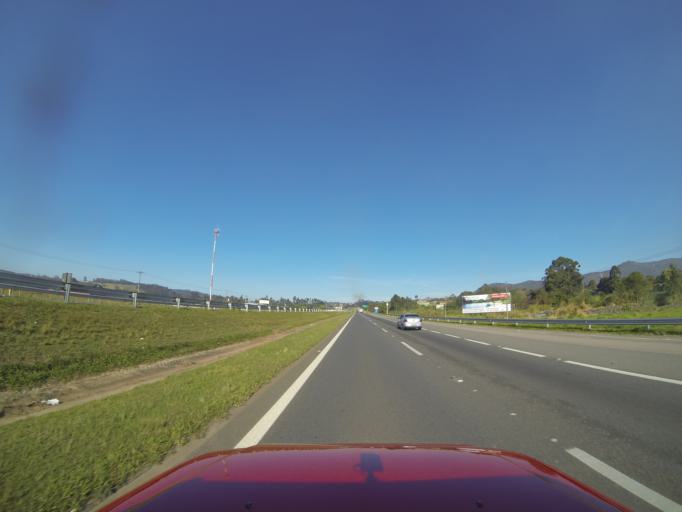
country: BR
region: Sao Paulo
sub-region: Atibaia
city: Atibaia
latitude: -23.1079
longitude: -46.5285
